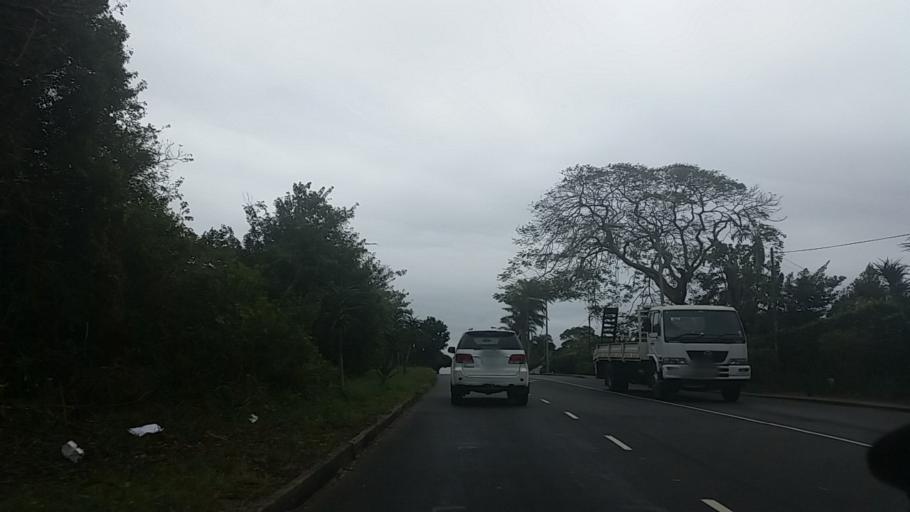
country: ZA
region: KwaZulu-Natal
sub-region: eThekwini Metropolitan Municipality
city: Berea
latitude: -29.8420
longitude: 30.9273
